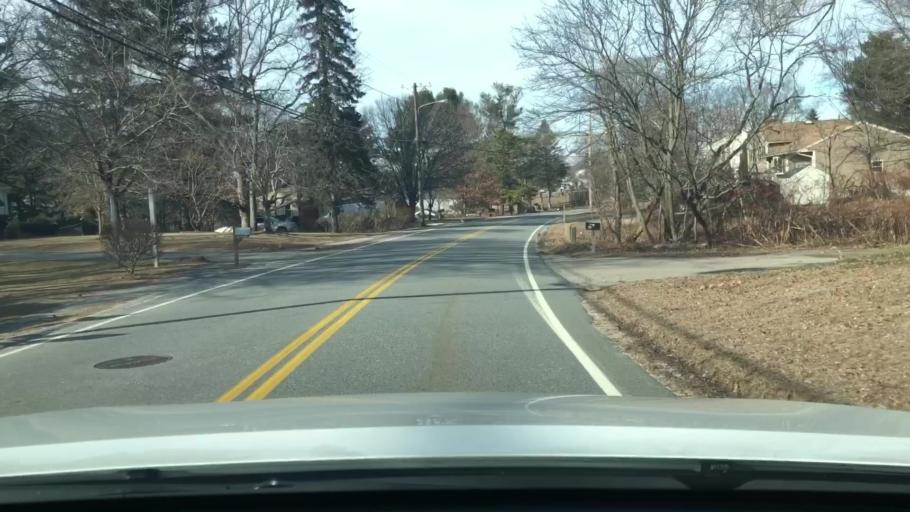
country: US
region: Massachusetts
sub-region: Worcester County
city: Blackstone
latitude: 42.0434
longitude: -71.5171
